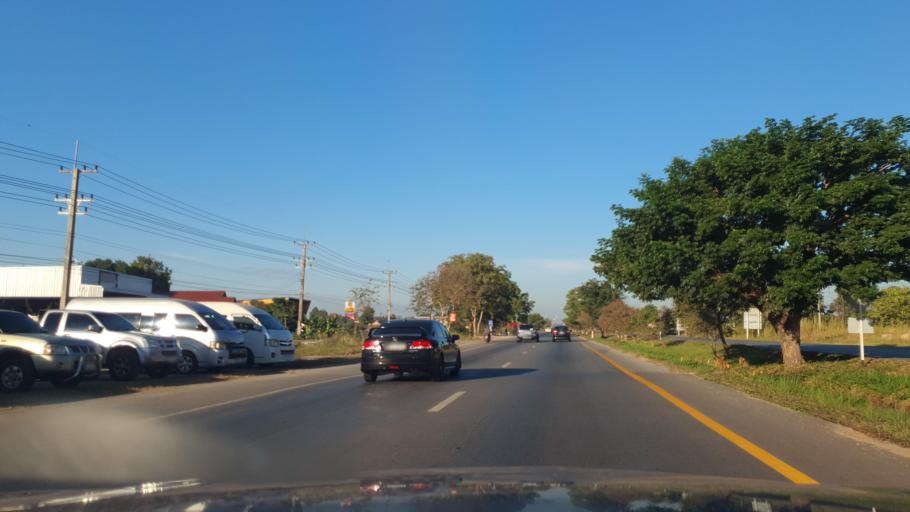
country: TH
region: Phitsanulok
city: Phitsanulok
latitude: 16.8643
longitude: 100.2752
